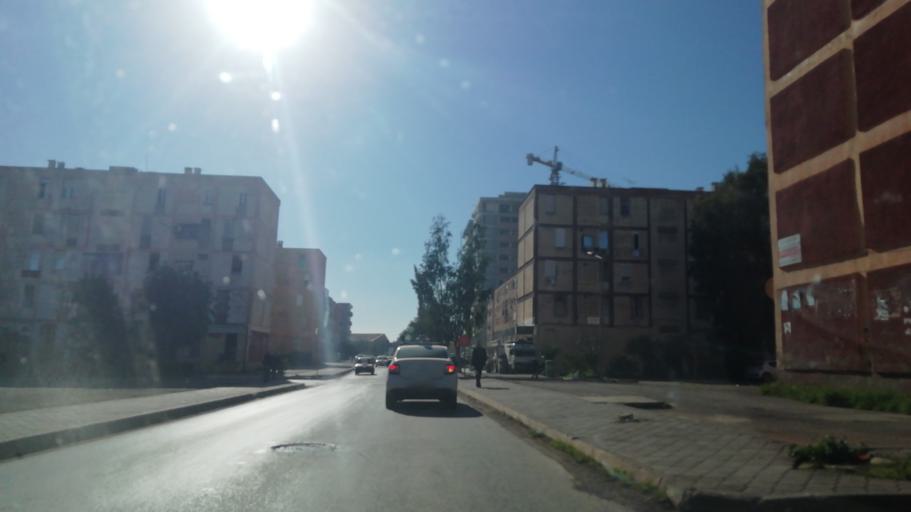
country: DZ
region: Oran
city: Oran
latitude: 35.6681
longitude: -0.6477
